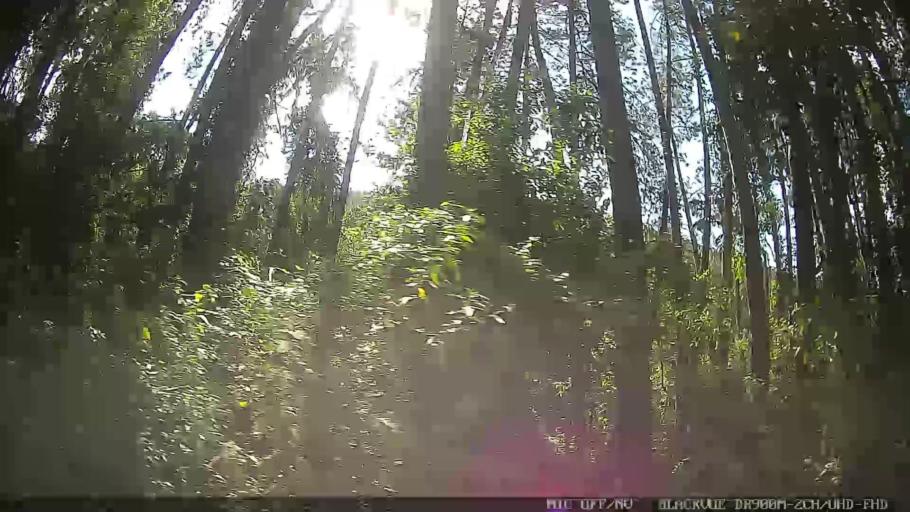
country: BR
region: Sao Paulo
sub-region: Bom Jesus Dos Perdoes
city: Bom Jesus dos Perdoes
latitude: -23.1659
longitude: -46.5129
